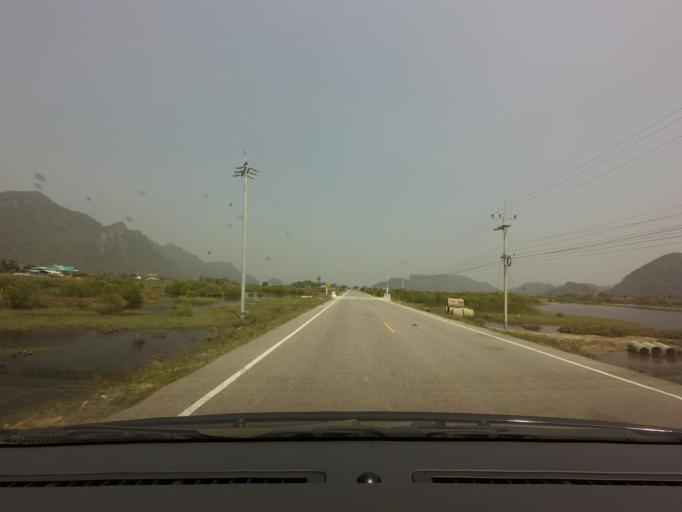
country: TH
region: Prachuap Khiri Khan
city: Sam Roi Yot
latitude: 12.1822
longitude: 99.9754
